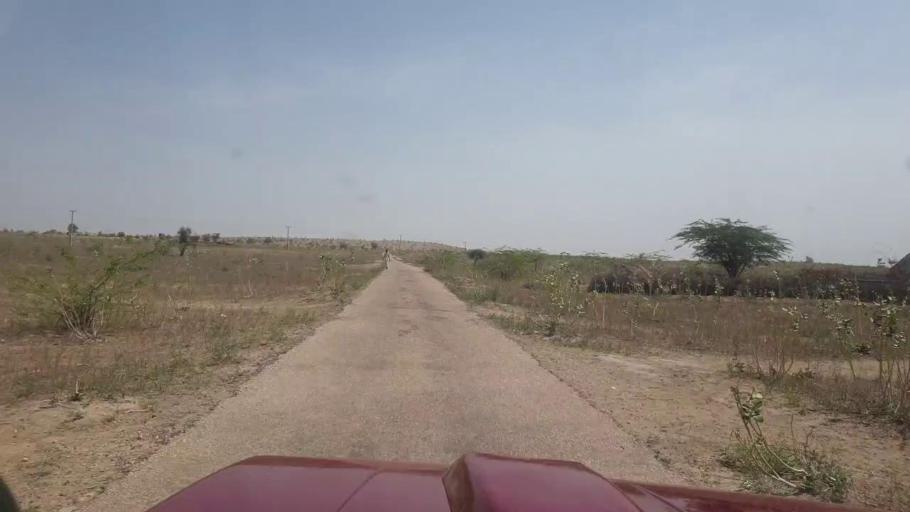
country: PK
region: Sindh
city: Islamkot
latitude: 25.1244
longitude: 70.3812
